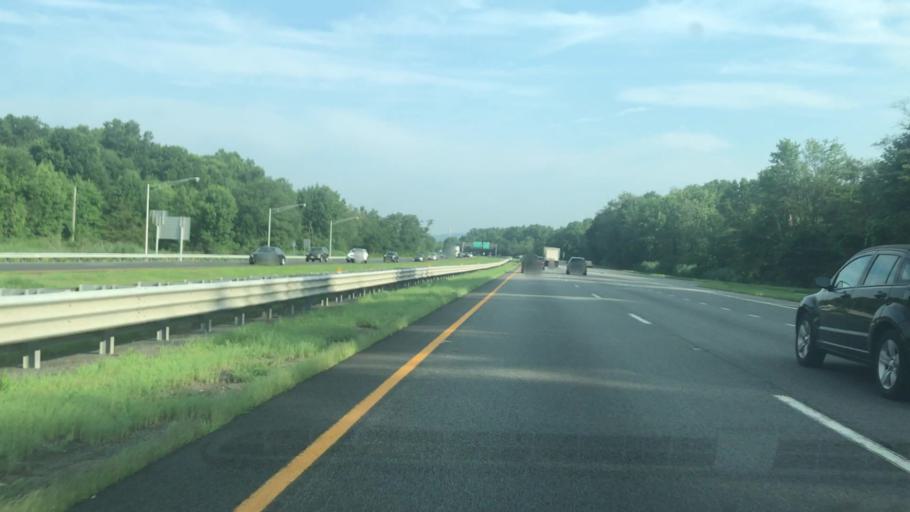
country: US
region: New Jersey
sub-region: Morris County
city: East Hanover
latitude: 40.8502
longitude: -74.3541
